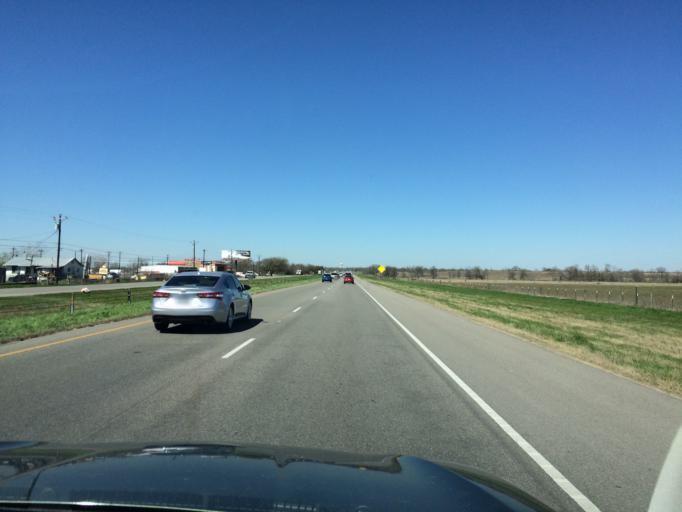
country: US
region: Texas
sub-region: Travis County
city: Garfield
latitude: 30.1771
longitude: -97.5305
